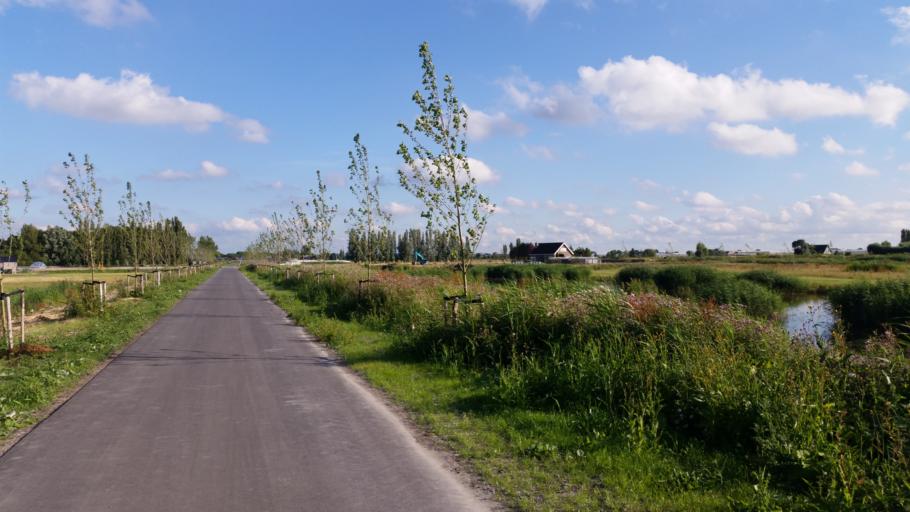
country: NL
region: South Holland
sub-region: Gemeente Lansingerland
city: Berkel en Rodenrijs
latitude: 52.0247
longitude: 4.4777
